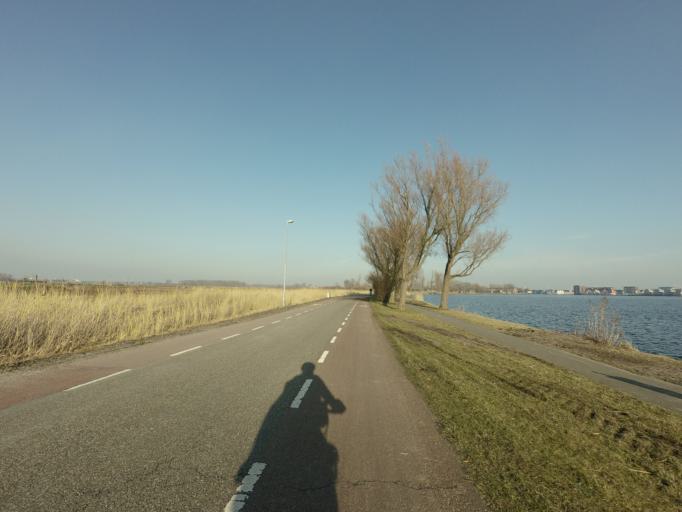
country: NL
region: North Holland
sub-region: Gemeente Haarlem
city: Haarlem
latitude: 52.4096
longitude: 4.6673
